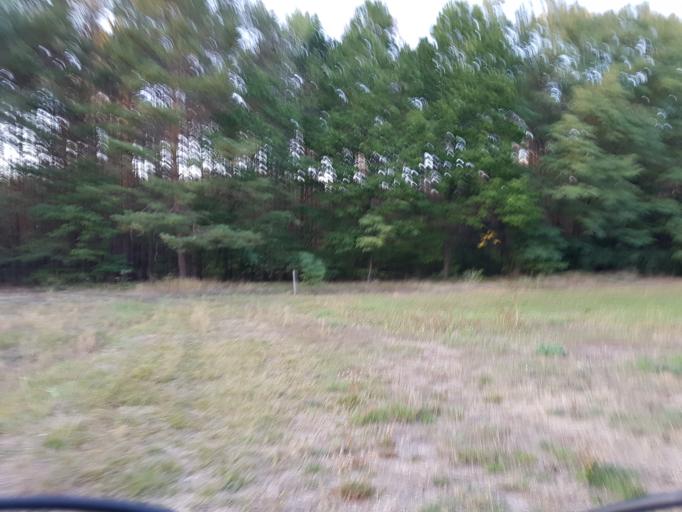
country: DE
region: Brandenburg
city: Trobitz
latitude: 51.5539
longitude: 13.4284
